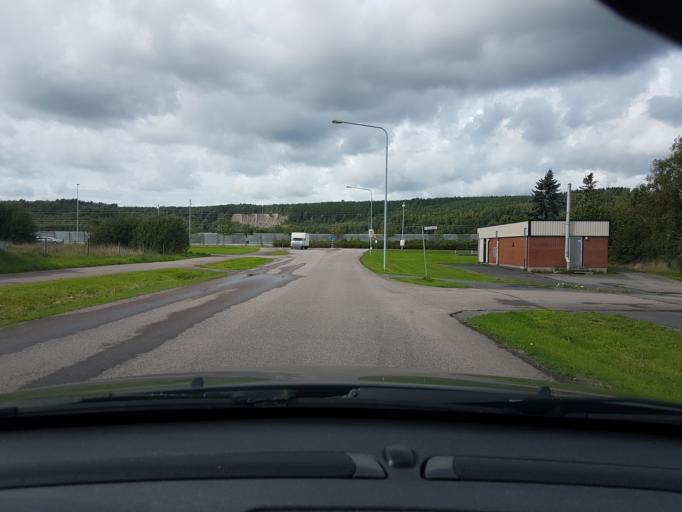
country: SE
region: Vaestra Goetaland
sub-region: Ale Kommun
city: Nodinge-Nol
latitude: 57.9088
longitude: 12.0550
